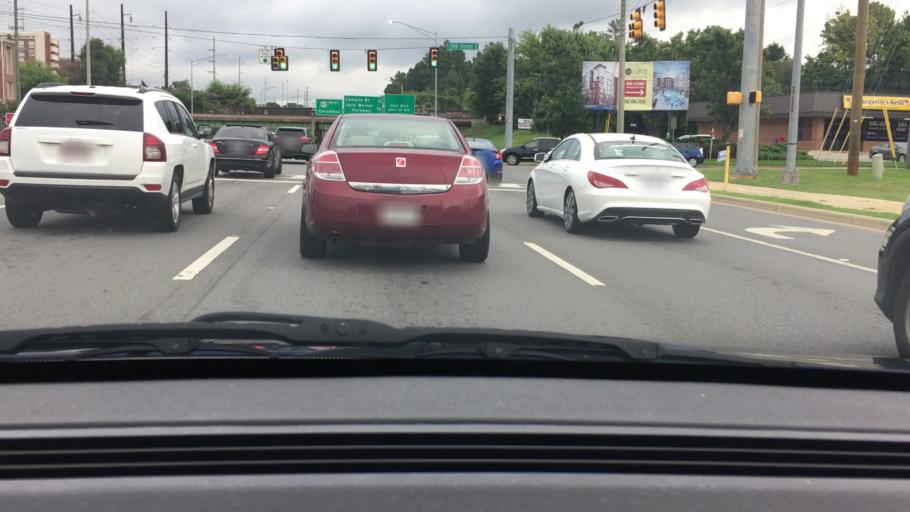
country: US
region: Alabama
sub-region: Tuscaloosa County
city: Tuscaloosa
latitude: 33.2004
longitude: -87.5253
